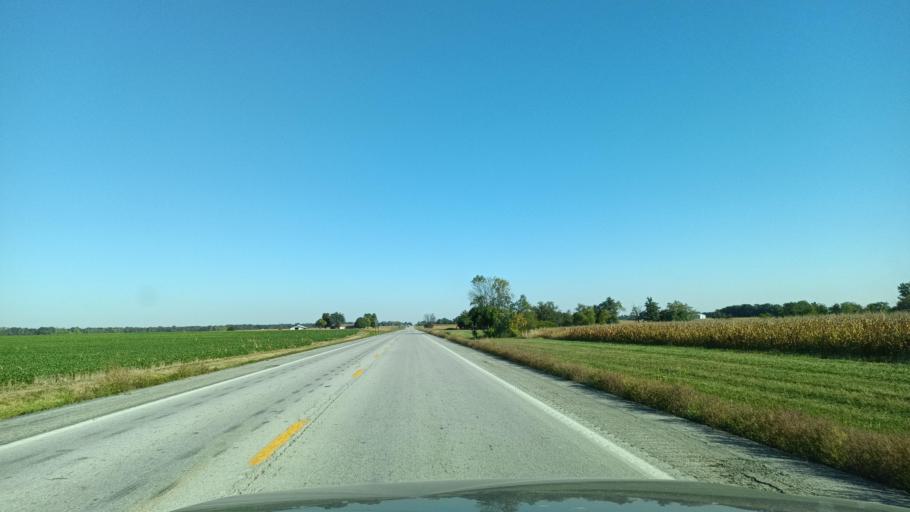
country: US
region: Missouri
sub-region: Audrain County
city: Vandalia
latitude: 39.2859
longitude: -91.6441
